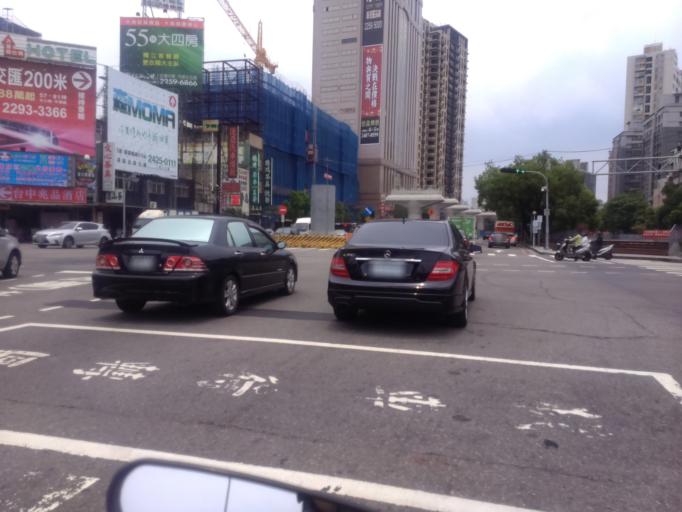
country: TW
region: Taiwan
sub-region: Taichung City
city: Taichung
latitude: 24.1738
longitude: 120.6712
